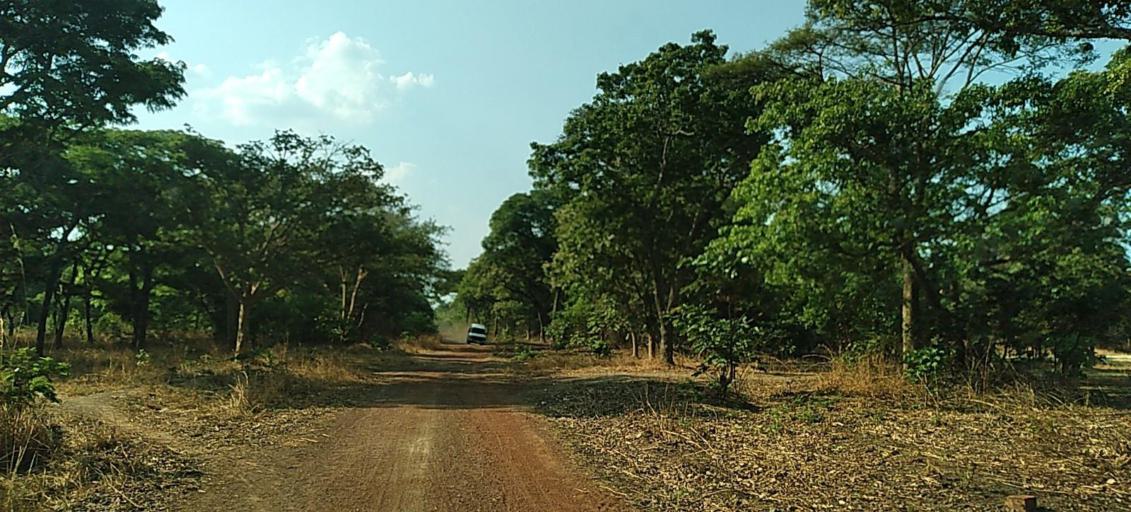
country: ZM
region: Copperbelt
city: Mpongwe
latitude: -13.4518
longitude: 28.0659
